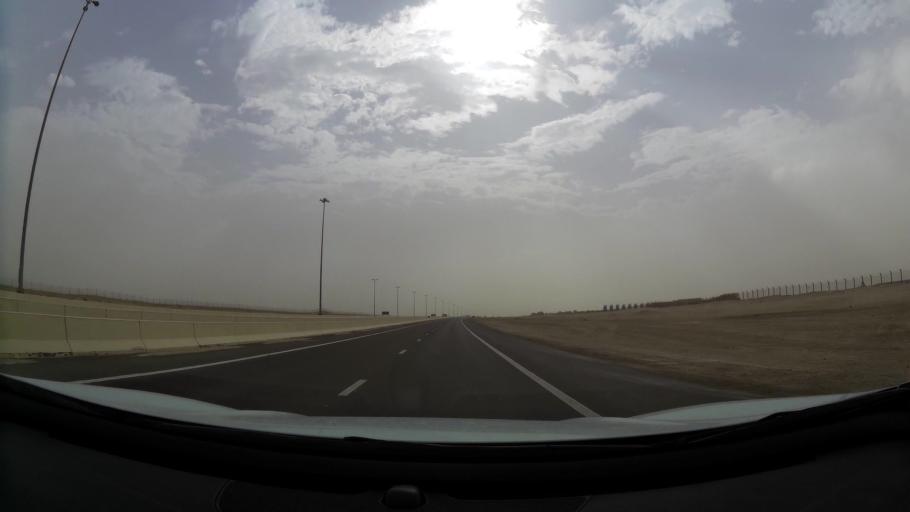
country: AE
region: Abu Dhabi
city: Abu Dhabi
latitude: 24.4789
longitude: 54.6622
